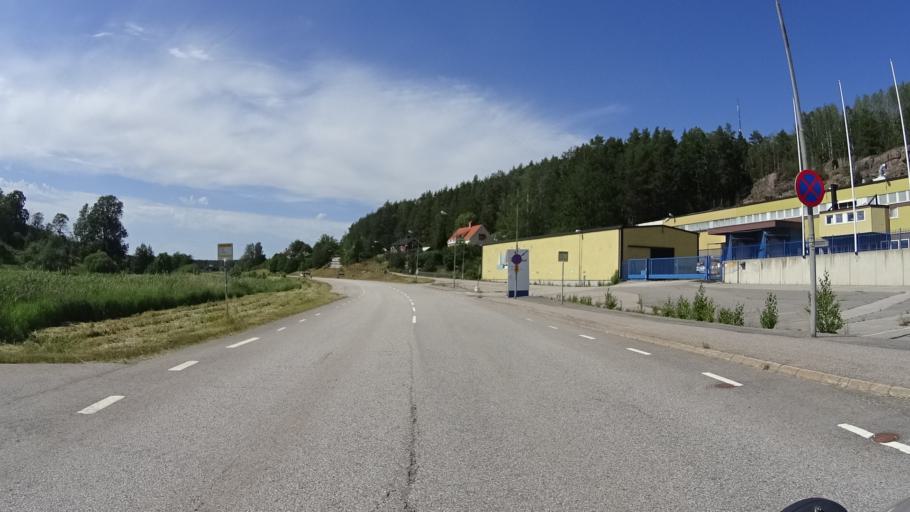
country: SE
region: Kalmar
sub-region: Vasterviks Kommun
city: Gamleby
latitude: 57.9036
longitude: 16.3980
